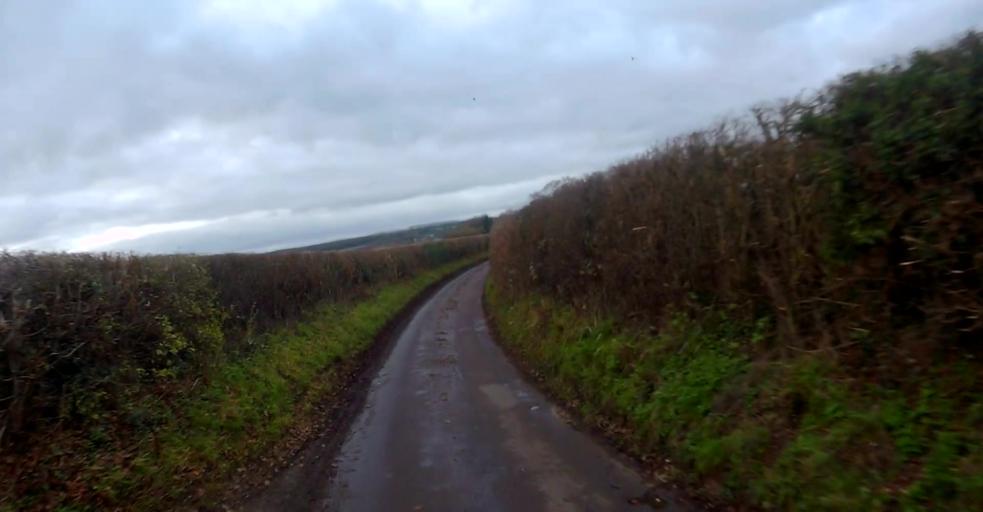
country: GB
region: England
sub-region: Hampshire
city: Overton
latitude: 51.2344
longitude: -1.2508
